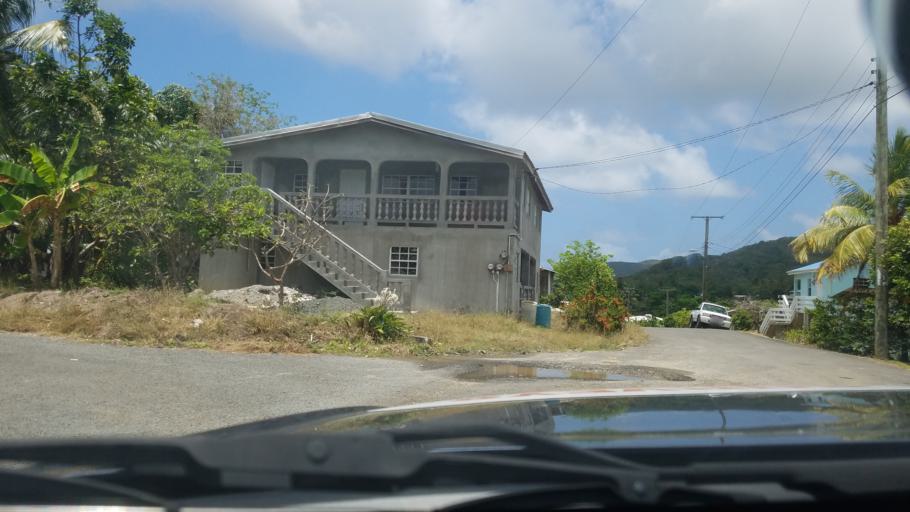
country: LC
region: Gros-Islet
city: Gros Islet
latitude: 14.0555
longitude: -60.9310
